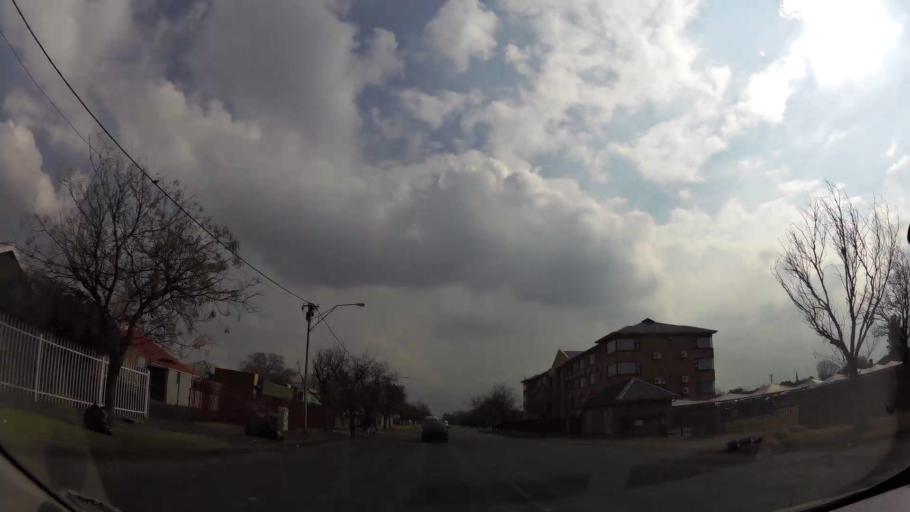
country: ZA
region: Gauteng
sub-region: Sedibeng District Municipality
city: Vereeniging
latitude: -26.6715
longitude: 27.9272
